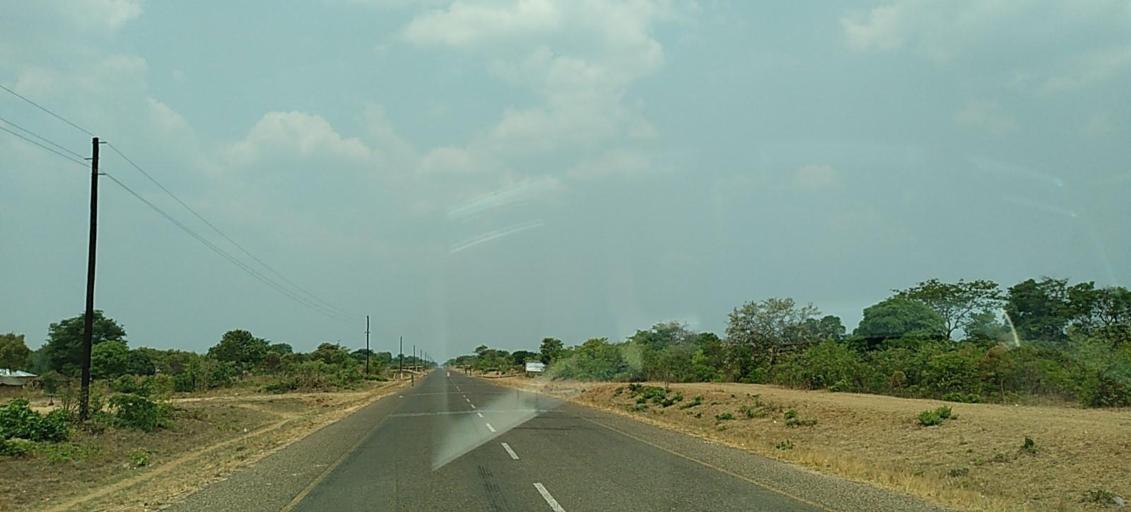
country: ZM
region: North-Western
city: Zambezi
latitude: -13.5514
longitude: 23.1287
